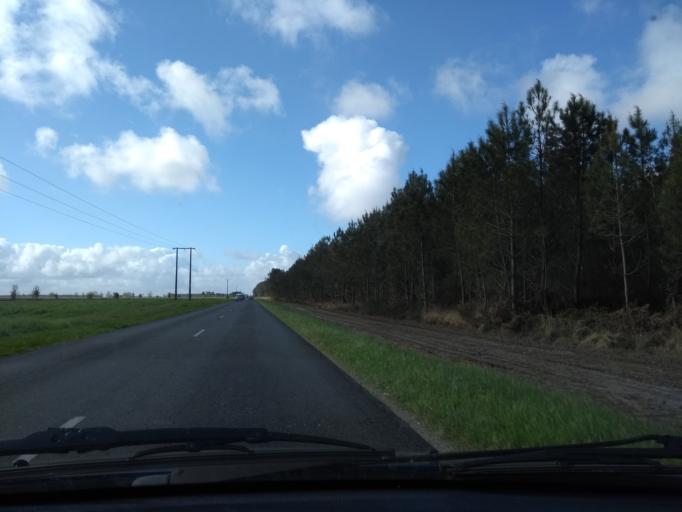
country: FR
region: Aquitaine
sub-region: Departement des Landes
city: Sanguinet
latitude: 44.4301
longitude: -1.0728
